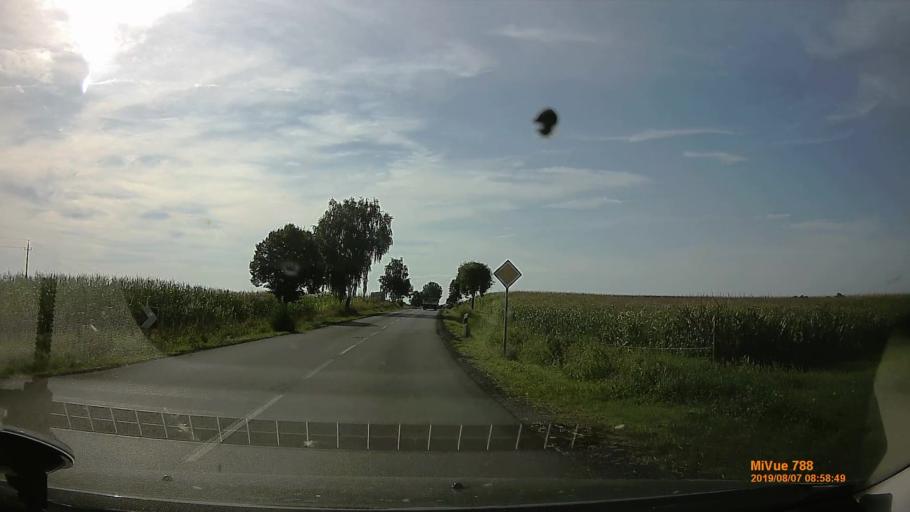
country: HU
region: Zala
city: Pacsa
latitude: 46.7411
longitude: 16.9304
